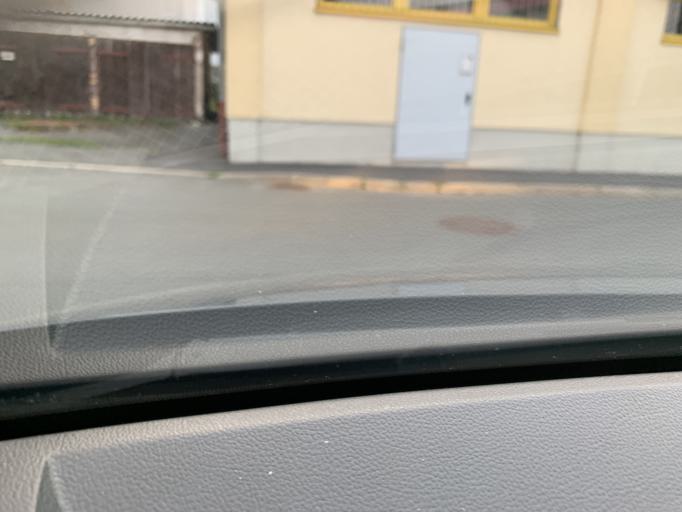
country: DE
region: Thuringia
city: Steinach
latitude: 50.4297
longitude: 11.1607
